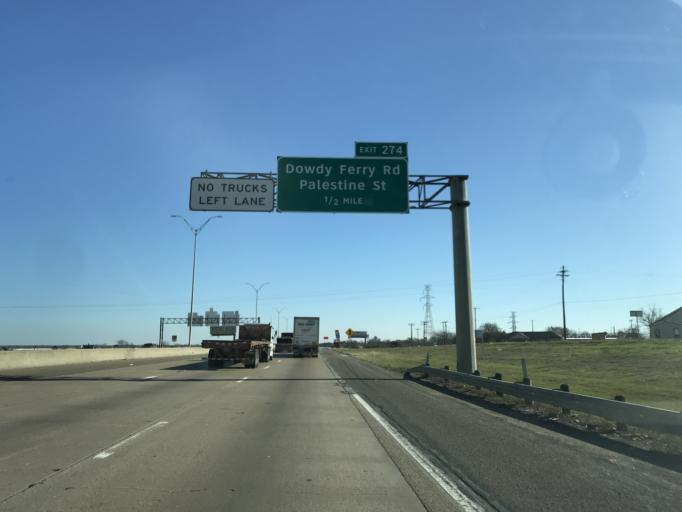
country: US
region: Texas
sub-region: Dallas County
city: Hutchins
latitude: 32.6570
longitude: -96.7193
